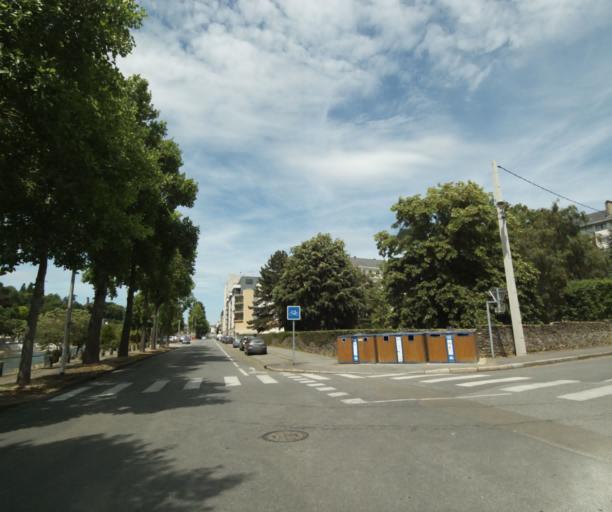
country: FR
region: Pays de la Loire
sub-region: Departement de la Mayenne
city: Laval
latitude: 48.0625
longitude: -0.7638
